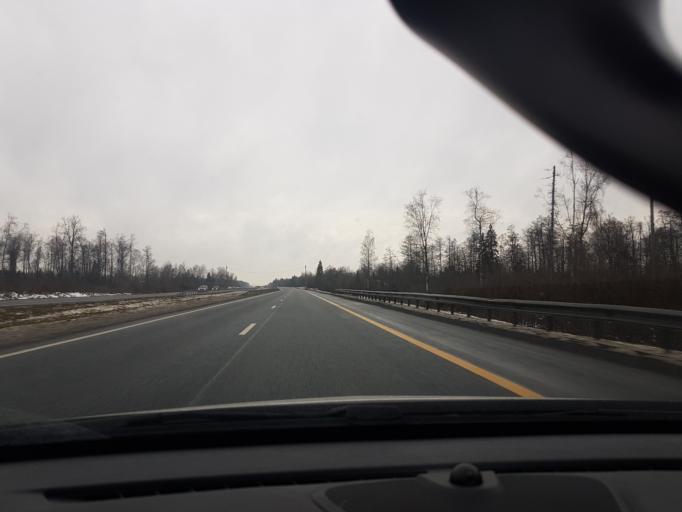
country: RU
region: Moskovskaya
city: Novopetrovskoye
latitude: 55.9817
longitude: 36.4285
